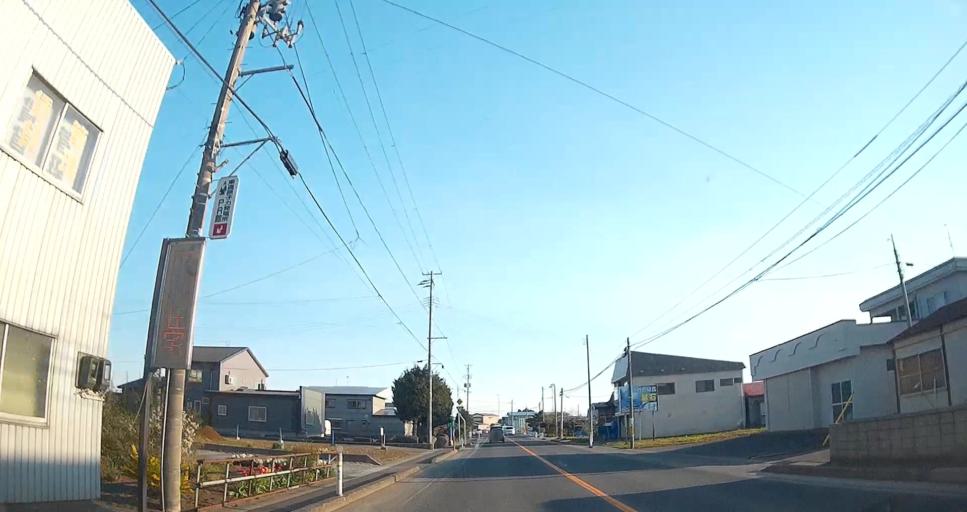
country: JP
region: Aomori
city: Mutsu
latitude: 41.2812
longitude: 141.2098
